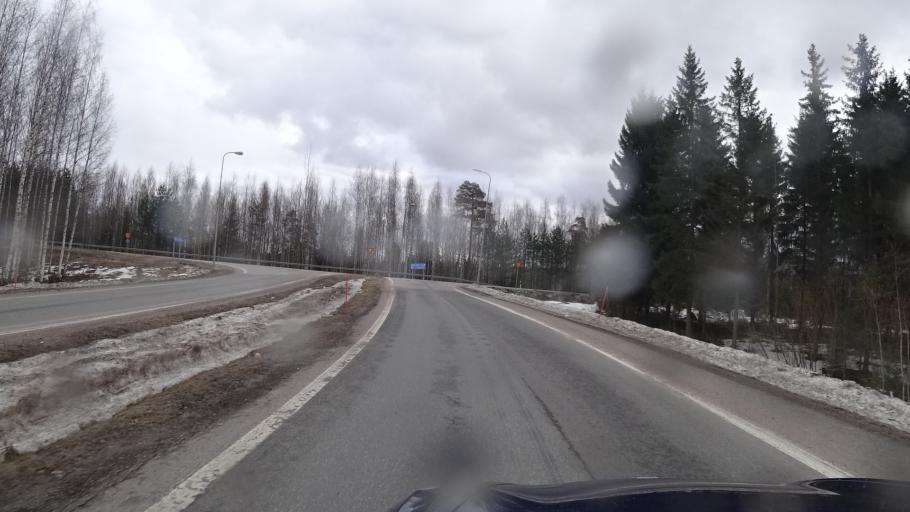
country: FI
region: Paijanne Tavastia
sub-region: Lahti
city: Nastola
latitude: 60.9205
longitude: 25.9984
